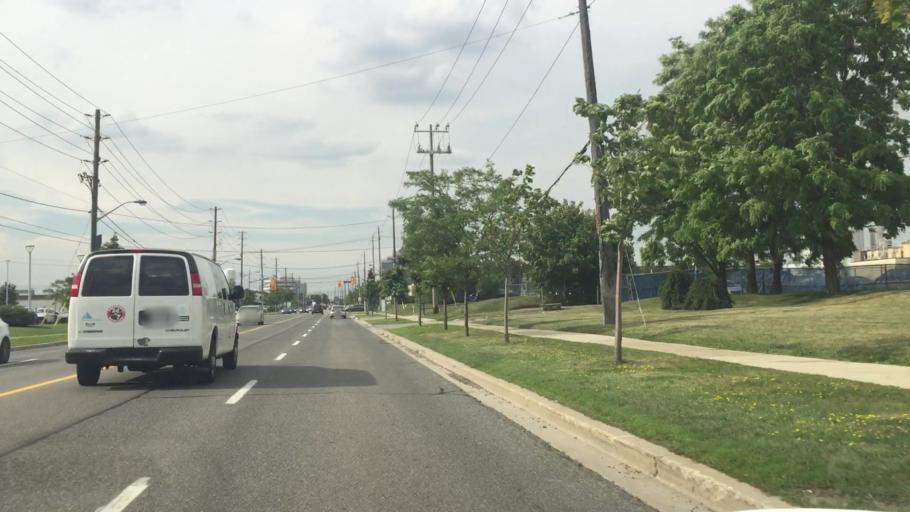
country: CA
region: Ontario
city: Concord
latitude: 43.7644
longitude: -79.5406
